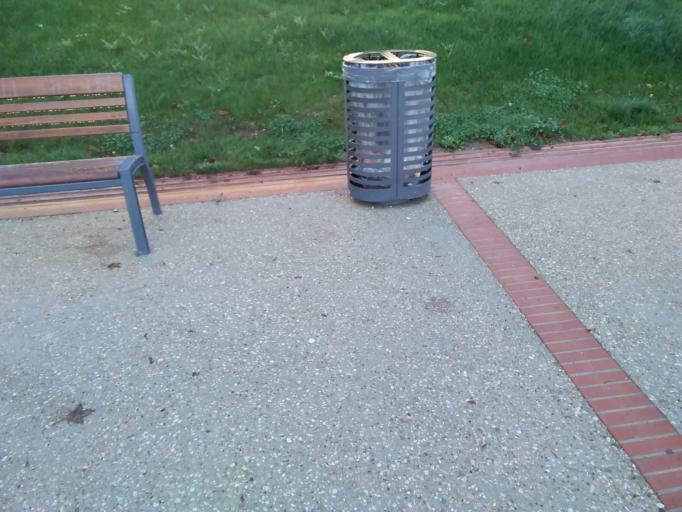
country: FR
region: Picardie
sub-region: Departement de la Somme
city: Amiens
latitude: 49.9038
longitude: 2.3005
